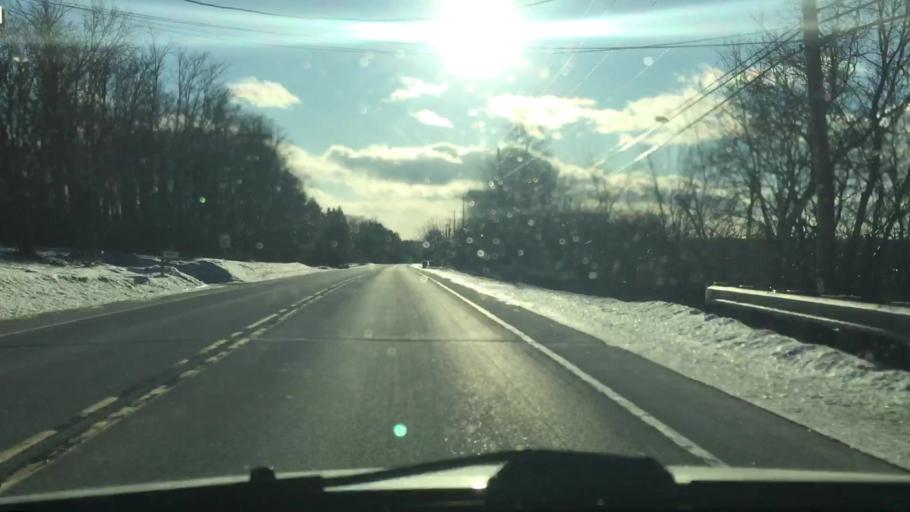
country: US
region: Wisconsin
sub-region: Waukesha County
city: Muskego
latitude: 42.9421
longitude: -88.1635
